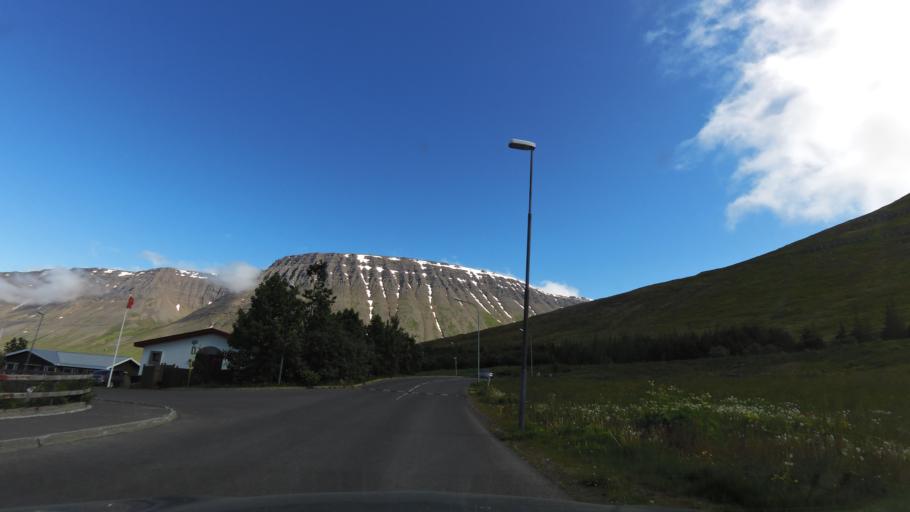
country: IS
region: Westfjords
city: Isafjoerdur
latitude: 66.0546
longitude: -23.1747
